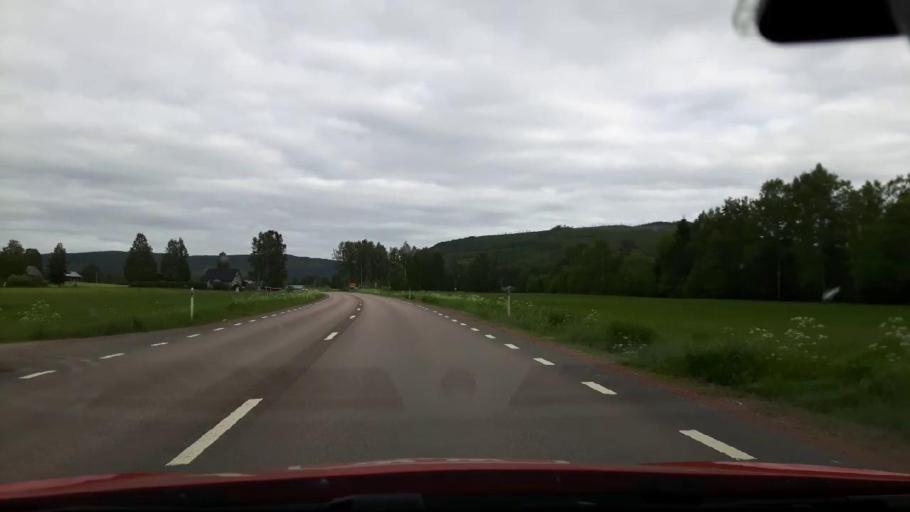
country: SE
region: Jaemtland
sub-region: Ragunda Kommun
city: Hammarstrand
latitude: 63.1512
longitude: 16.2547
